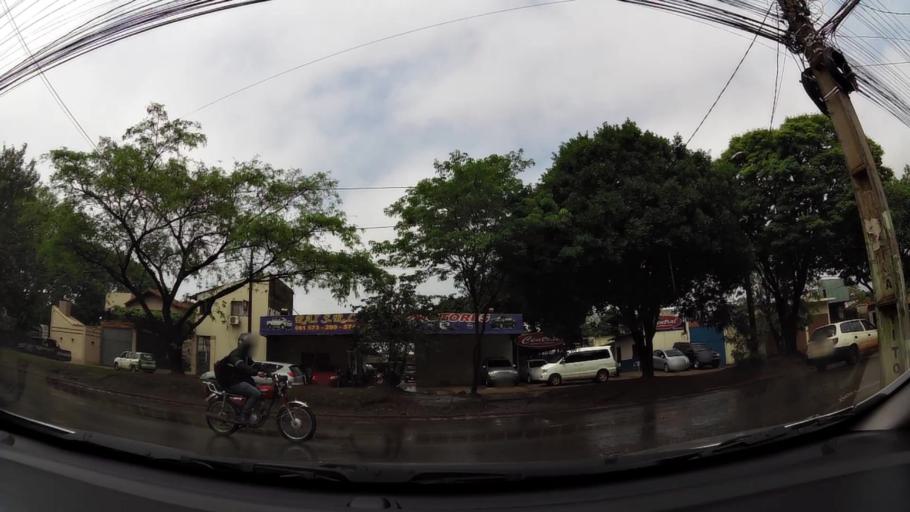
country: PY
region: Alto Parana
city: Presidente Franco
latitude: -25.5150
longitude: -54.6455
